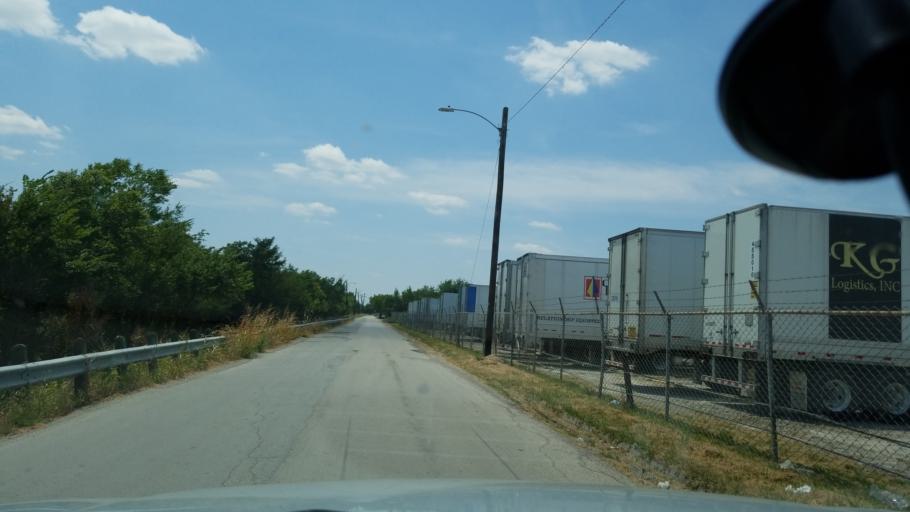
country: US
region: Texas
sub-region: Dallas County
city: Grand Prairie
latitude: 32.7464
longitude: -96.9734
